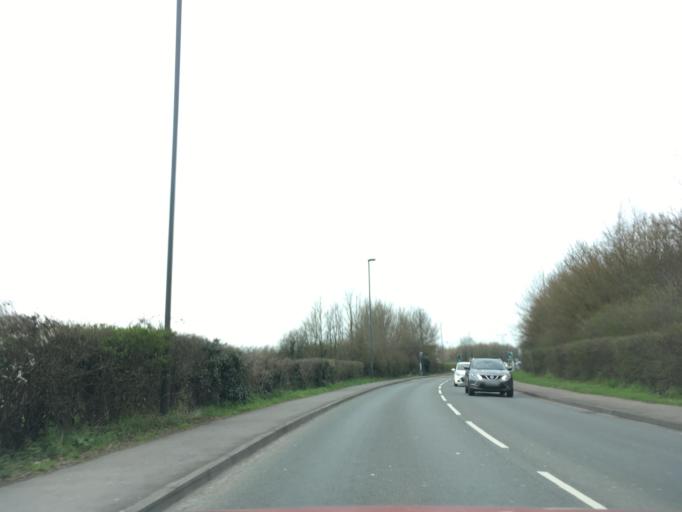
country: GB
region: England
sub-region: South Gloucestershire
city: Stoke Gifford
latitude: 51.5197
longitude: -2.5501
